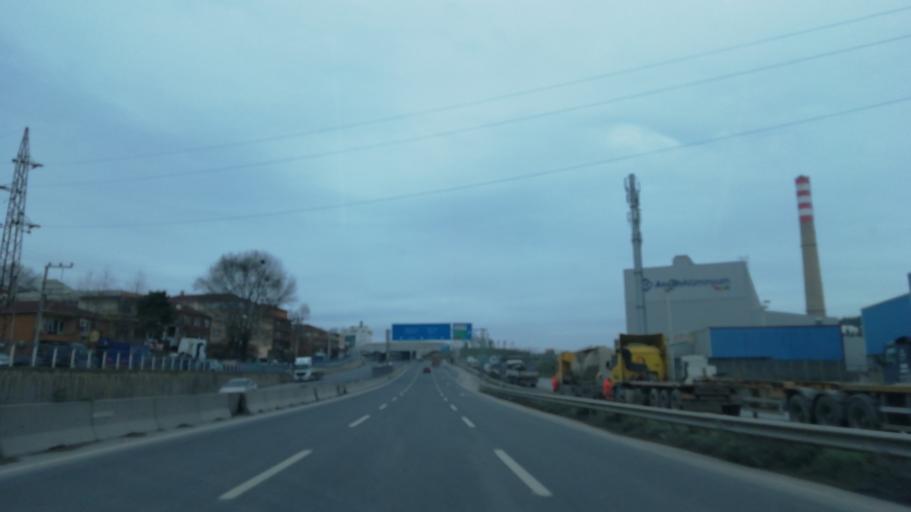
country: TR
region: Kocaeli
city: Tavsancil
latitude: 40.7828
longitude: 29.5379
